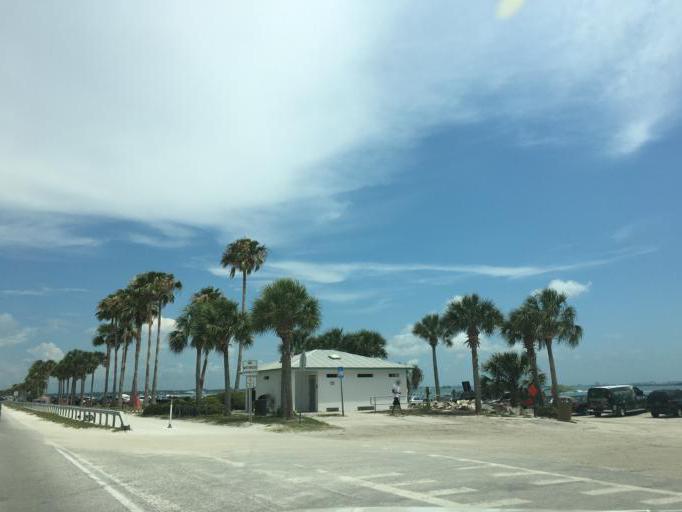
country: US
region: Florida
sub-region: Pinellas County
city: Palm Harbor
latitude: 28.0561
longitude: -82.8067
